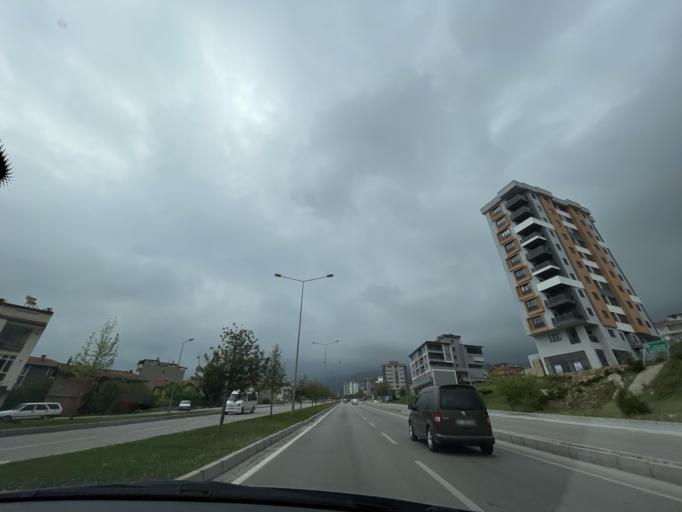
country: TR
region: Denizli
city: Denizli
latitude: 37.7324
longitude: 29.1450
